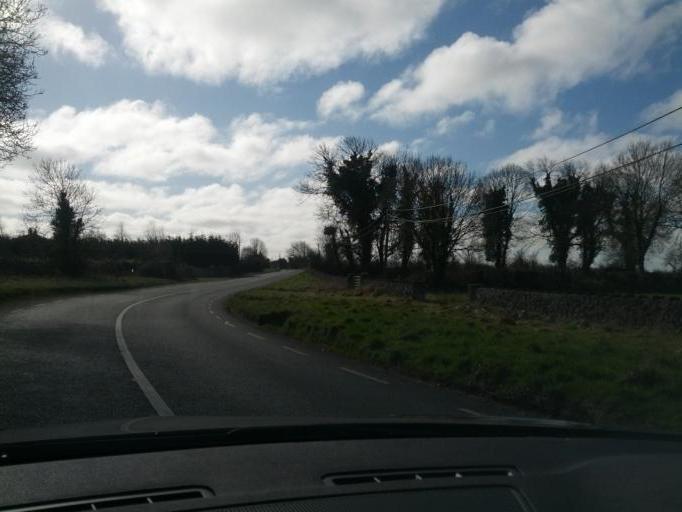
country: IE
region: Connaught
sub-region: County Galway
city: Ballinasloe
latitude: 53.4080
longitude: -8.3367
